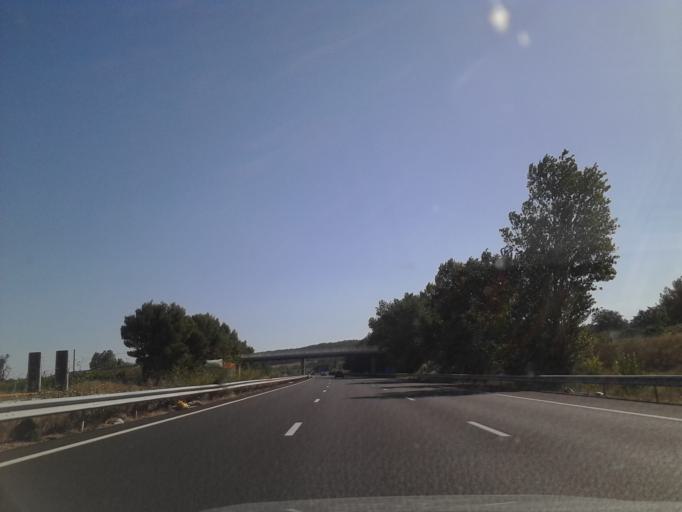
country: FR
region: Languedoc-Roussillon
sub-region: Departement de l'Aude
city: Vinassan
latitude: 43.1884
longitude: 3.0635
